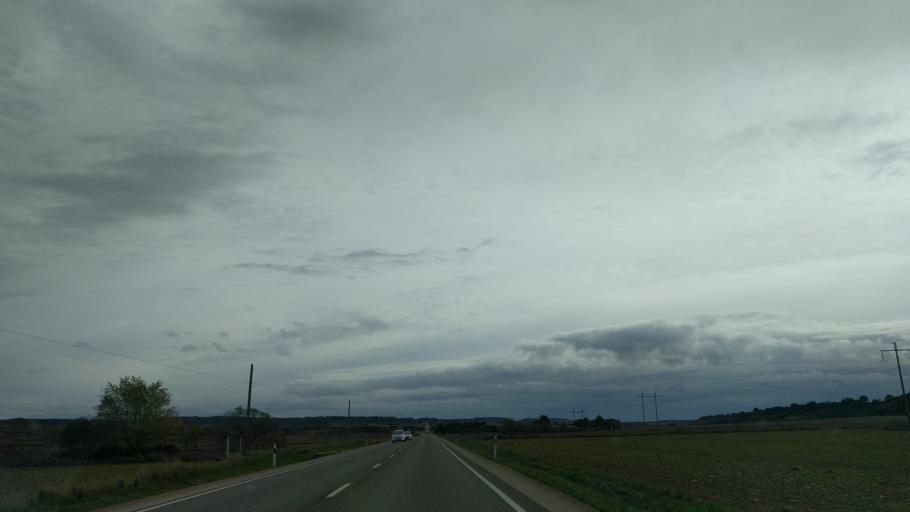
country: ES
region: Aragon
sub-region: Provincia de Huesca
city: Loporzano
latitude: 42.1403
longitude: -0.3214
